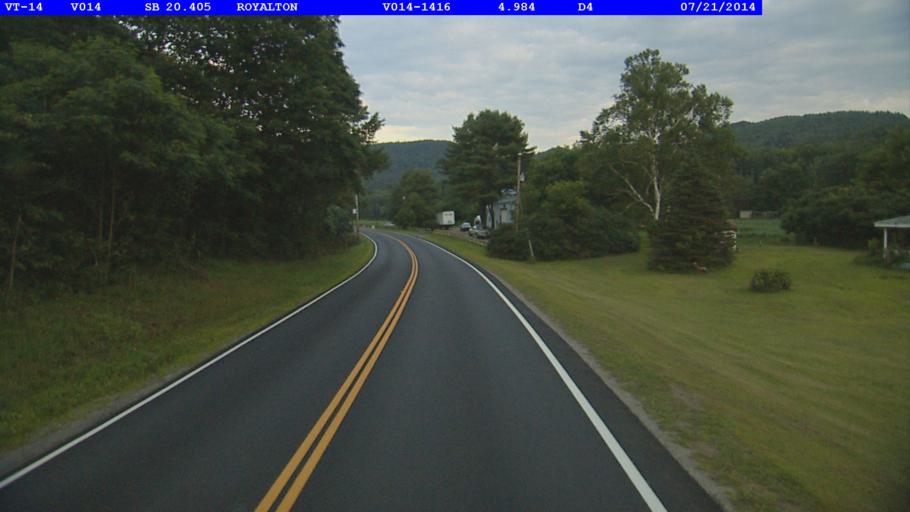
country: US
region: Vermont
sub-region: Orange County
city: Randolph
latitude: 43.8155
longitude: -72.5600
